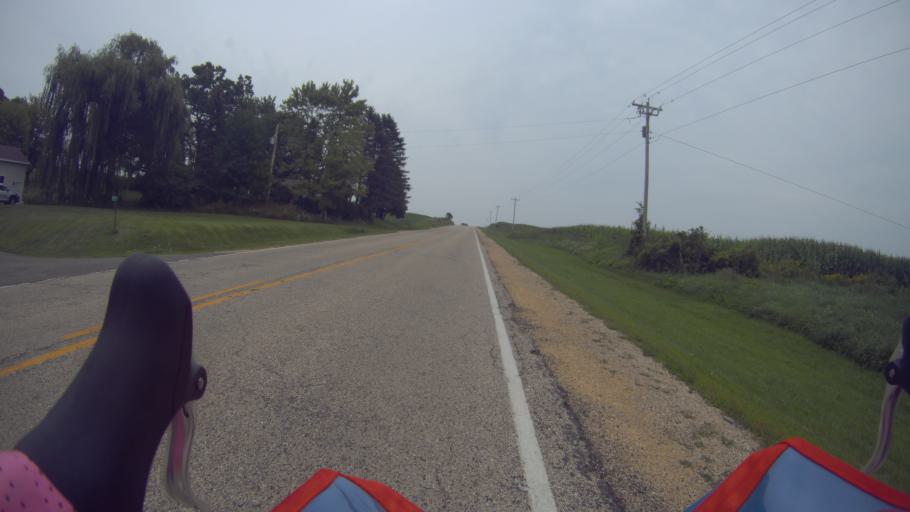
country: US
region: Wisconsin
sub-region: Dane County
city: Belleville
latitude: 42.9082
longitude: -89.5876
